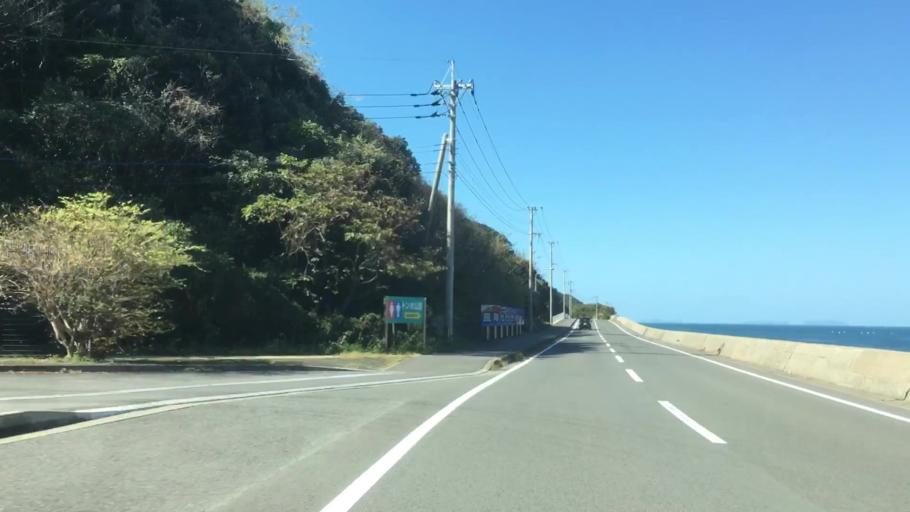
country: JP
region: Nagasaki
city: Sasebo
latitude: 33.0274
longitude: 129.5830
